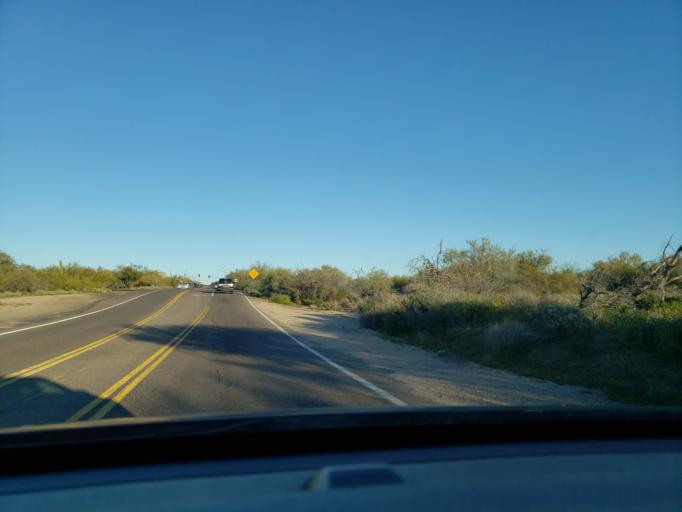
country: US
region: Arizona
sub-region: Maricopa County
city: Cave Creek
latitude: 33.7991
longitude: -111.9552
